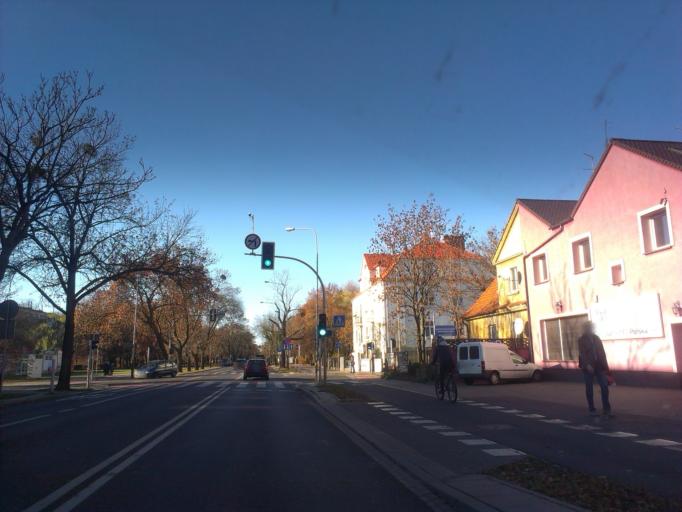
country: PL
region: Greater Poland Voivodeship
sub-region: Poznan
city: Poznan
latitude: 52.4102
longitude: 16.8841
